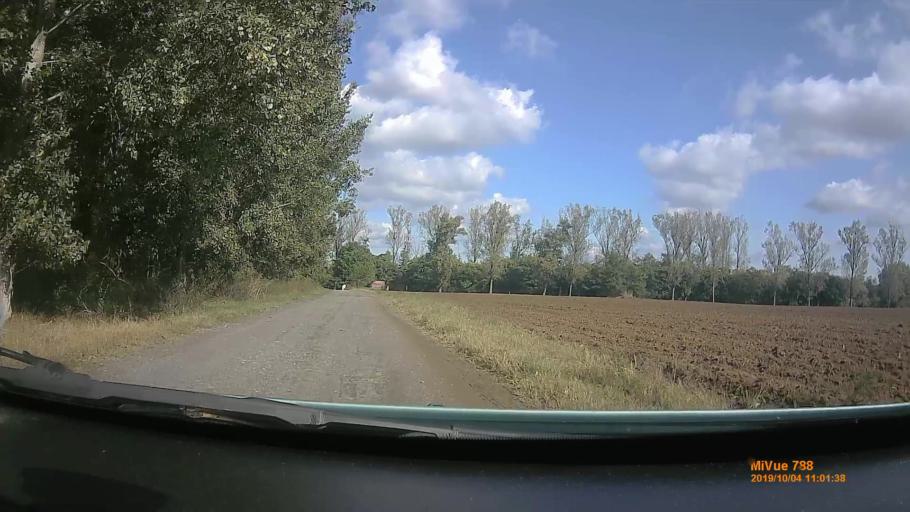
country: HU
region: Szabolcs-Szatmar-Bereg
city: Nyirtelek
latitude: 47.9842
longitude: 21.6722
